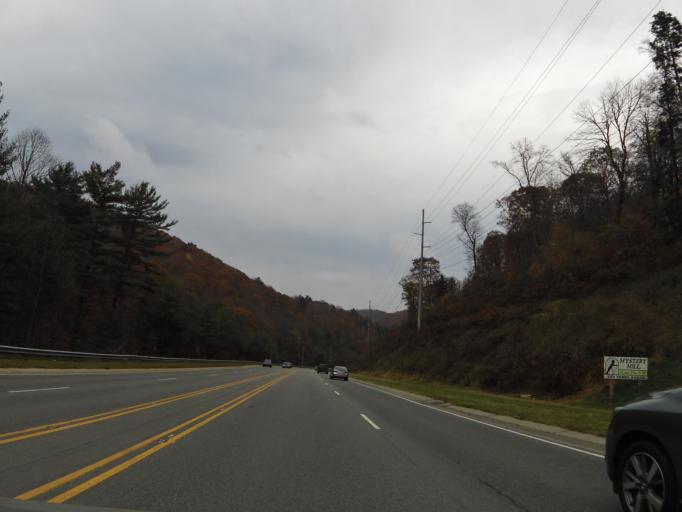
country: US
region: North Carolina
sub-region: Watauga County
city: Blowing Rock
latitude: 36.1735
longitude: -81.6477
